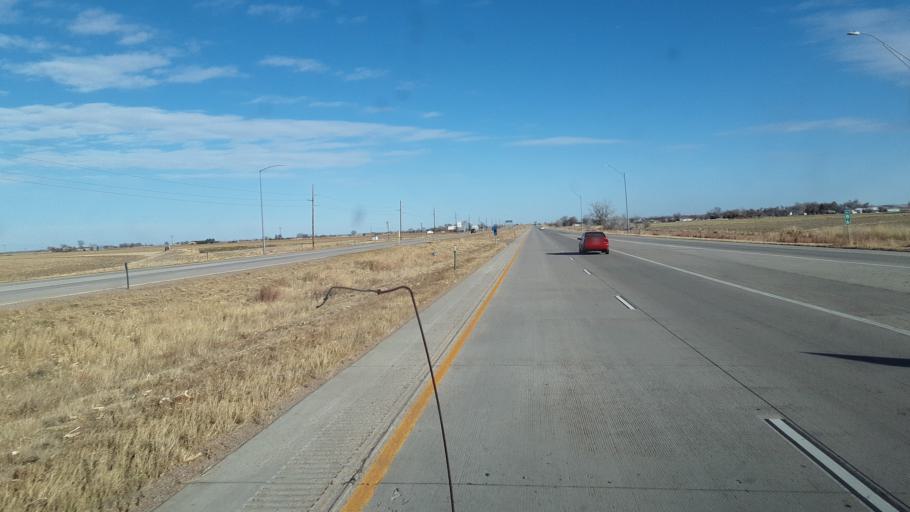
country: US
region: Colorado
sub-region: Morgan County
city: Brush
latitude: 40.2679
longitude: -103.6927
